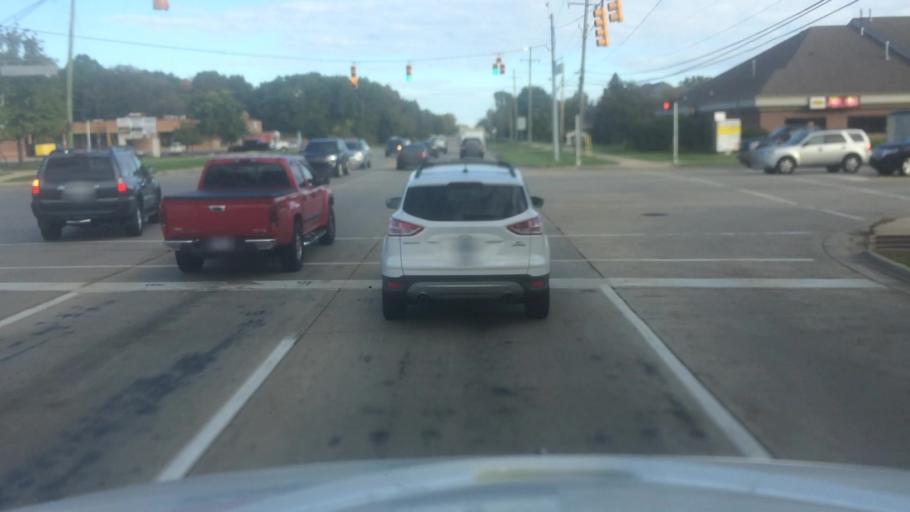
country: US
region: Michigan
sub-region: Macomb County
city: Shelby
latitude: 42.6555
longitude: -82.9940
